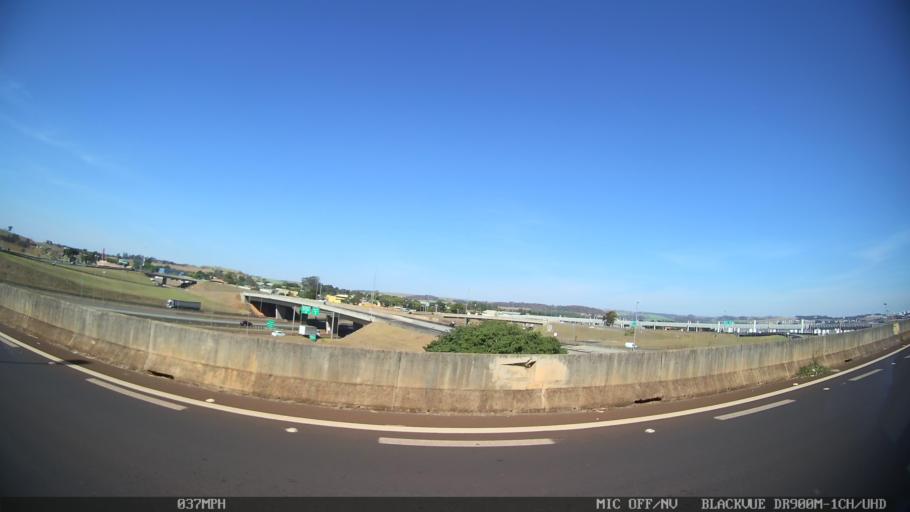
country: BR
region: Sao Paulo
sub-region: Ribeirao Preto
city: Ribeirao Preto
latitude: -21.2046
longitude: -47.7594
